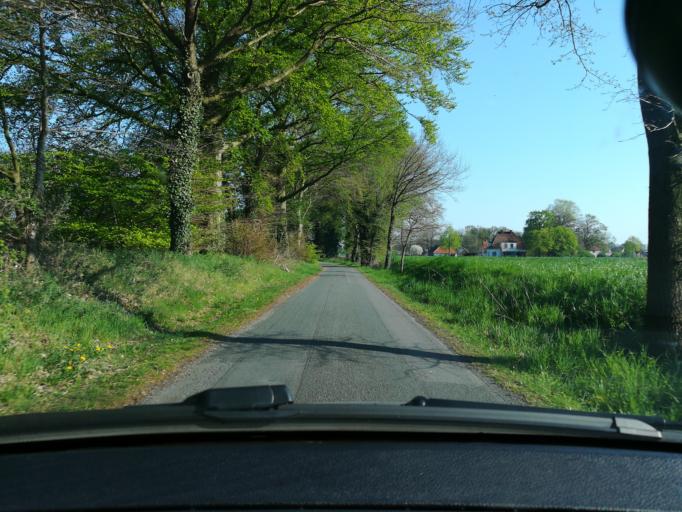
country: DE
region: North Rhine-Westphalia
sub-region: Regierungsbezirk Munster
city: Sassenberg
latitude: 52.0106
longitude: 8.0933
